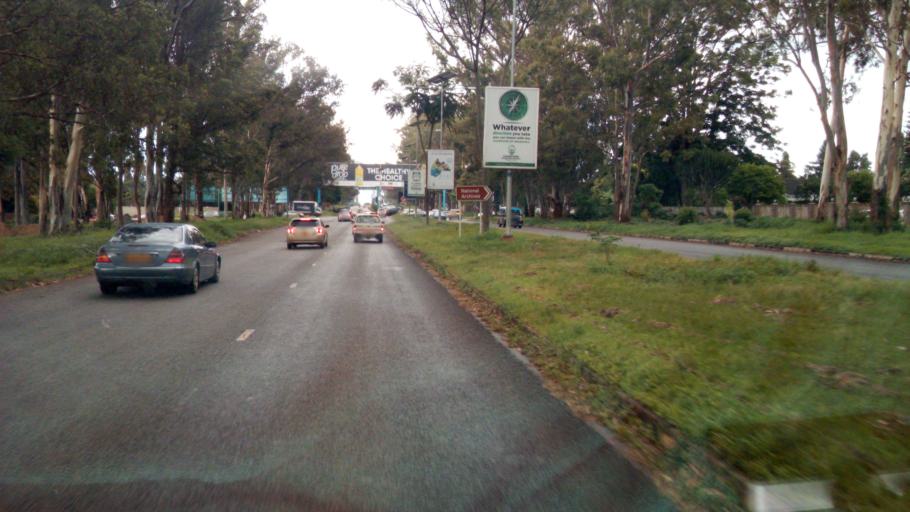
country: ZW
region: Harare
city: Harare
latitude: -17.7929
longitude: 31.0645
